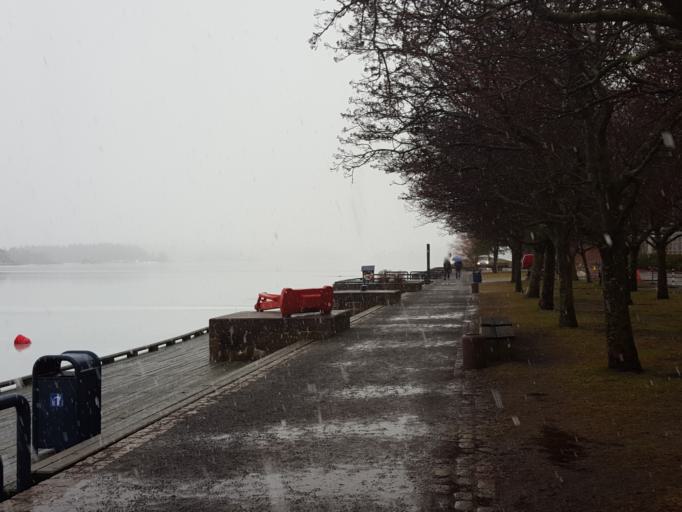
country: NO
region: Akershus
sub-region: Baerum
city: Sandvika
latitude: 59.8880
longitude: 10.5653
